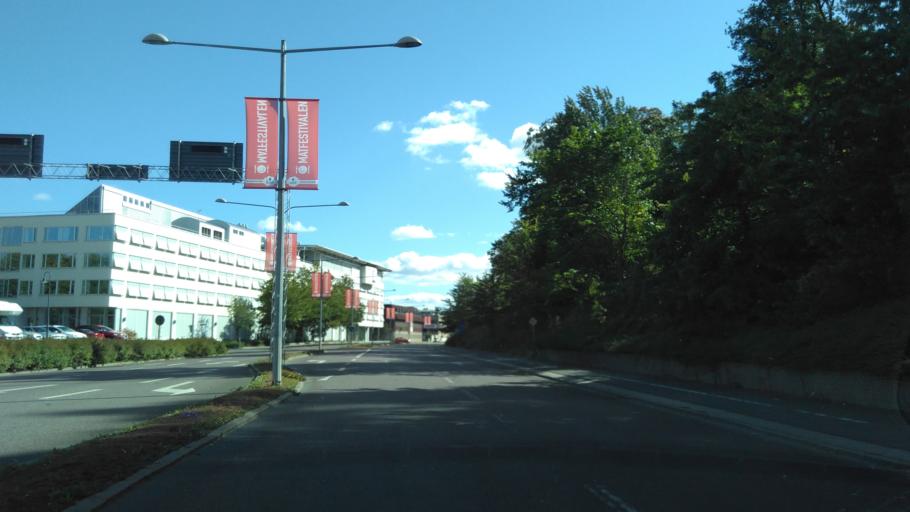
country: SE
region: Vaestra Goetaland
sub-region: Skovde Kommun
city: Skoevde
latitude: 58.3912
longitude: 13.8410
